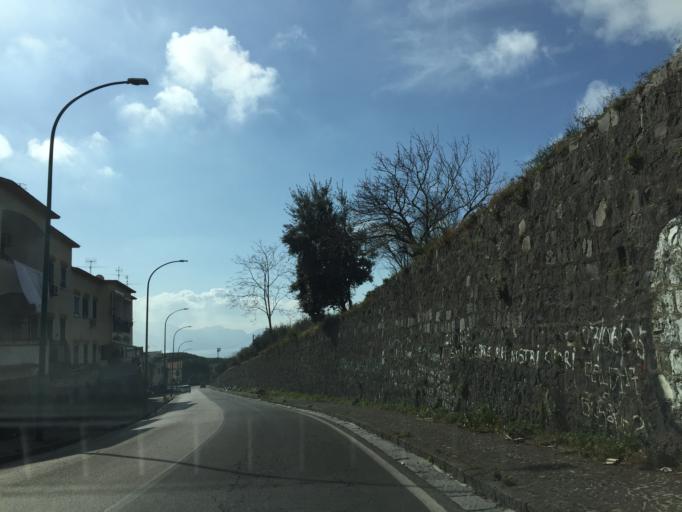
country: IT
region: Campania
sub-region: Provincia di Napoli
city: Torre del Greco
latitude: 40.7820
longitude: 14.4081
